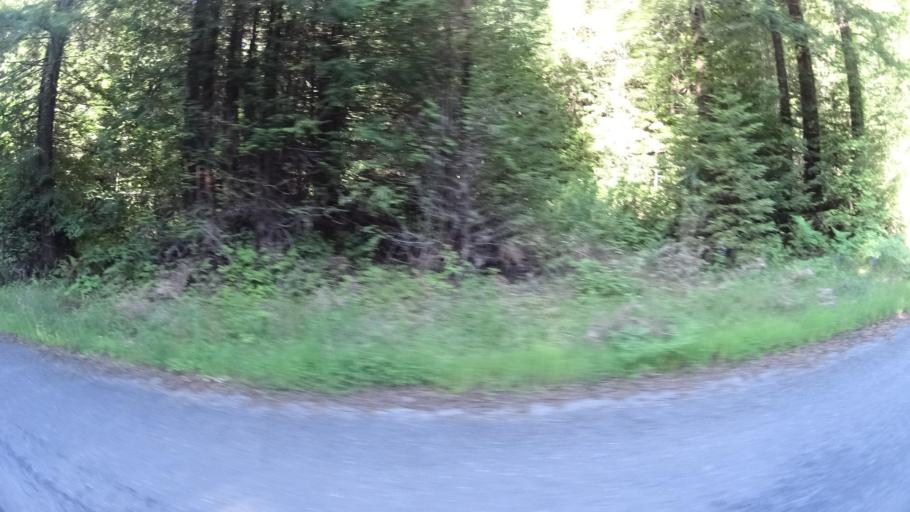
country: US
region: California
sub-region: Humboldt County
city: Rio Dell
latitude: 40.4395
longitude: -123.9704
